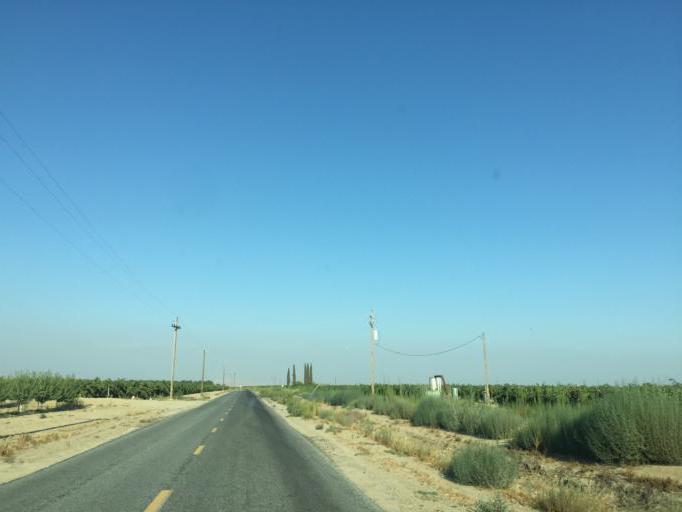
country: US
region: California
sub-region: Tulare County
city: London
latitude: 36.4584
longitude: -119.4264
